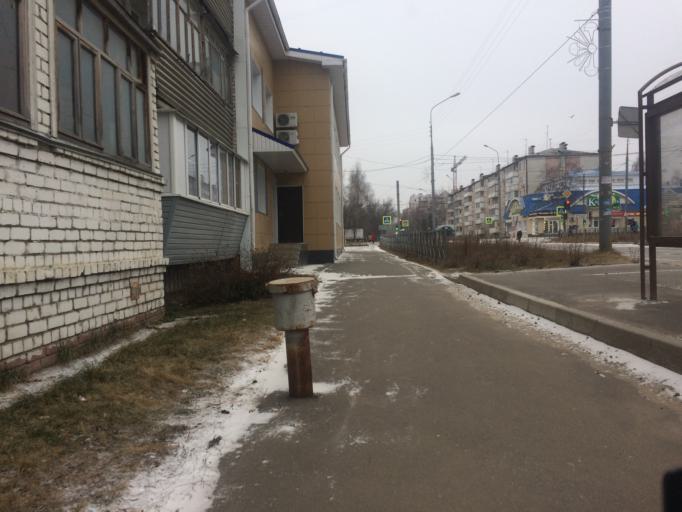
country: RU
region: Mariy-El
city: Yoshkar-Ola
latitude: 56.6505
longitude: 47.8640
